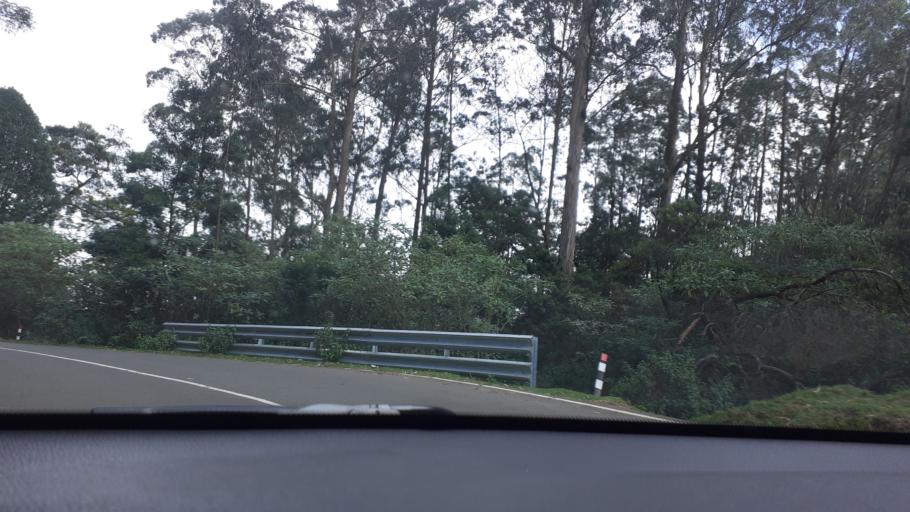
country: IN
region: Tamil Nadu
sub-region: Dindigul
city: Kodaikanal
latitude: 10.2359
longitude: 77.4251
